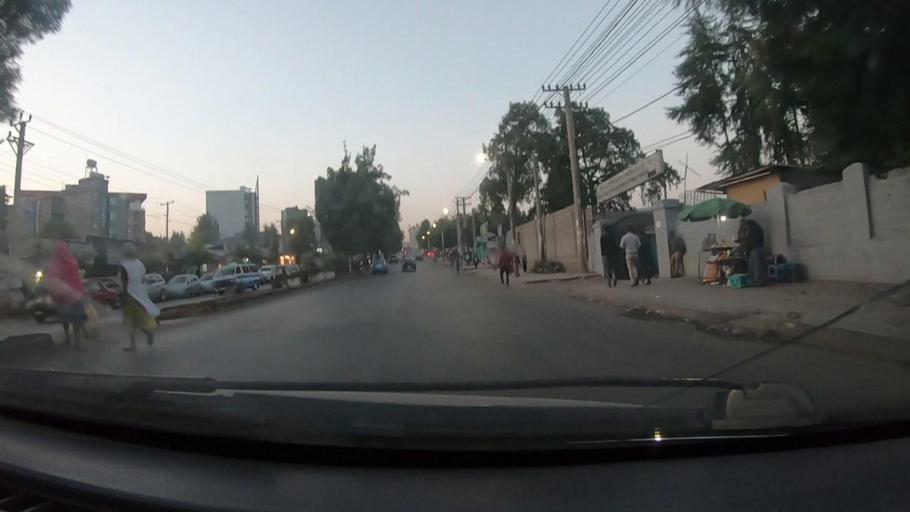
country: ET
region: Adis Abeba
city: Addis Ababa
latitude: 9.0459
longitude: 38.7477
